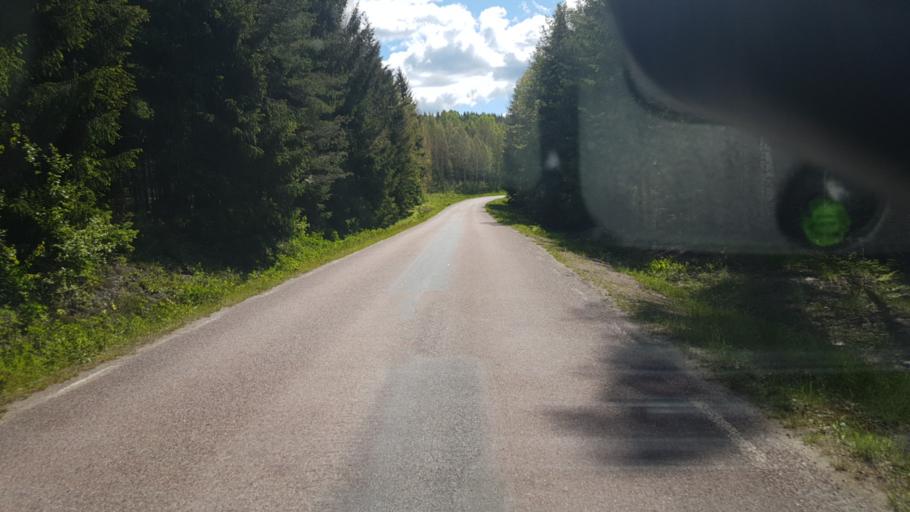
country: SE
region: Vaermland
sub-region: Arvika Kommun
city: Arvika
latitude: 59.5329
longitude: 12.8194
